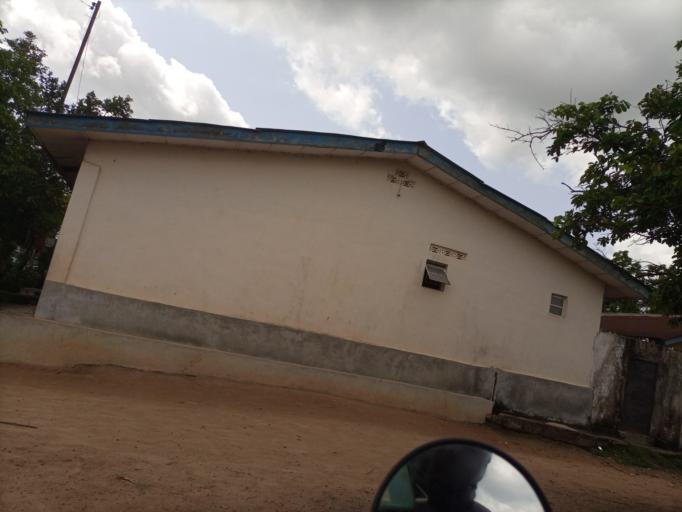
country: SL
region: Southern Province
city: Bo
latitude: 7.9477
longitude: -11.7318
